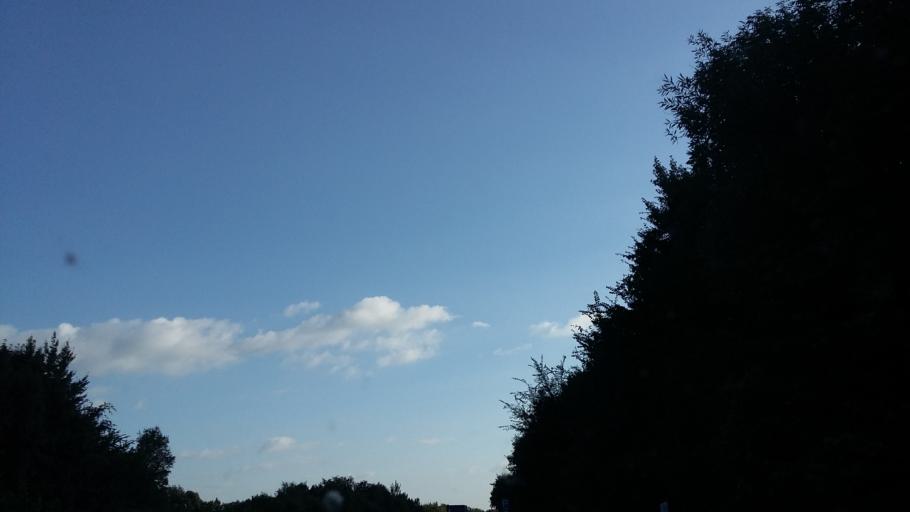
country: DE
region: Lower Saxony
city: Loxstedt
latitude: 53.4797
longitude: 8.6182
